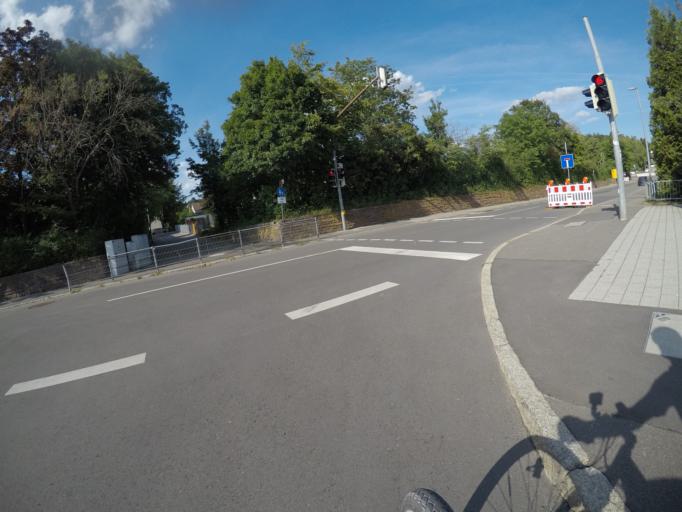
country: DE
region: Baden-Wuerttemberg
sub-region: Regierungsbezirk Stuttgart
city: Boeblingen
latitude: 48.6834
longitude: 9.0308
